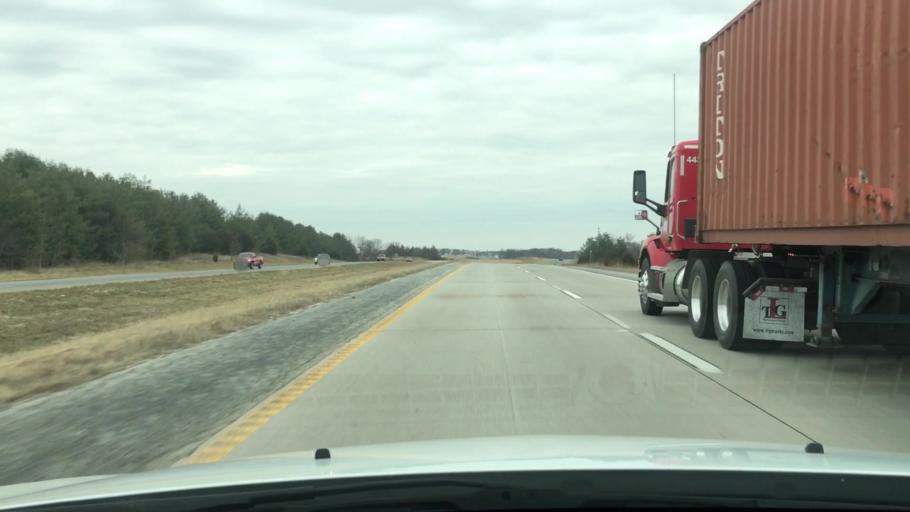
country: US
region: Missouri
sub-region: Audrain County
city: Mexico
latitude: 39.0942
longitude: -91.8990
